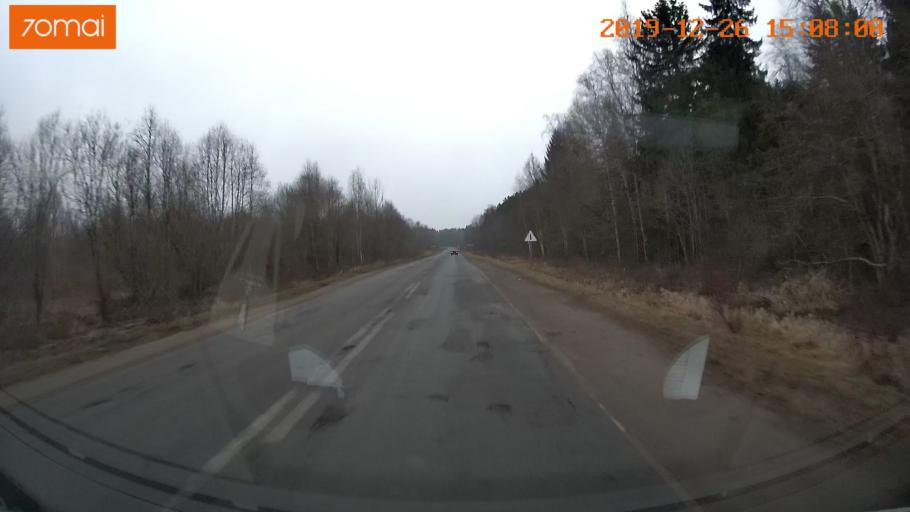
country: RU
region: Jaroslavl
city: Rybinsk
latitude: 58.1643
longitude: 38.8412
